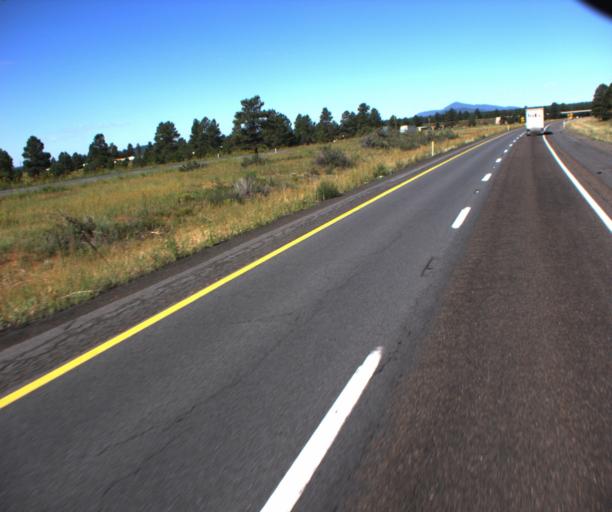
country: US
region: Arizona
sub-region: Coconino County
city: Parks
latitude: 35.2482
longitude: -111.9718
